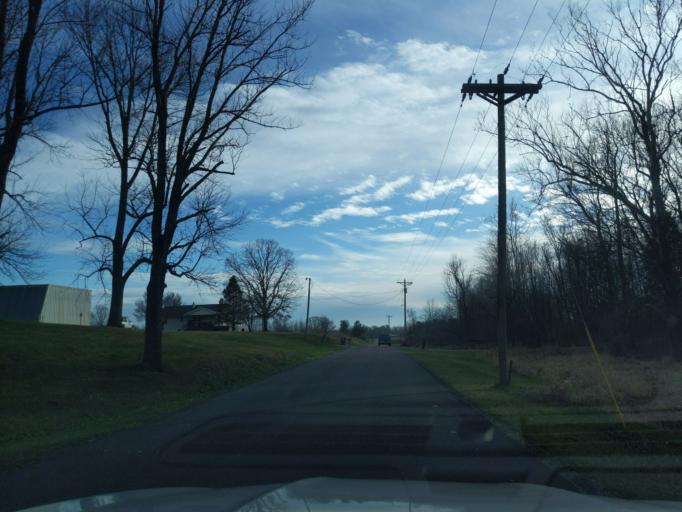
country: US
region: Indiana
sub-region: Decatur County
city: Westport
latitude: 39.1899
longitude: -85.5457
